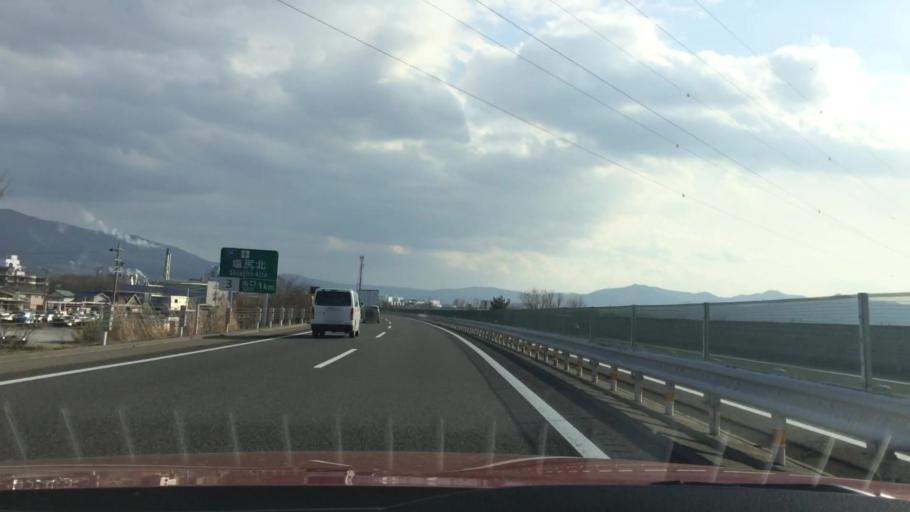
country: JP
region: Nagano
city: Matsumoto
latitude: 36.1752
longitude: 137.9423
